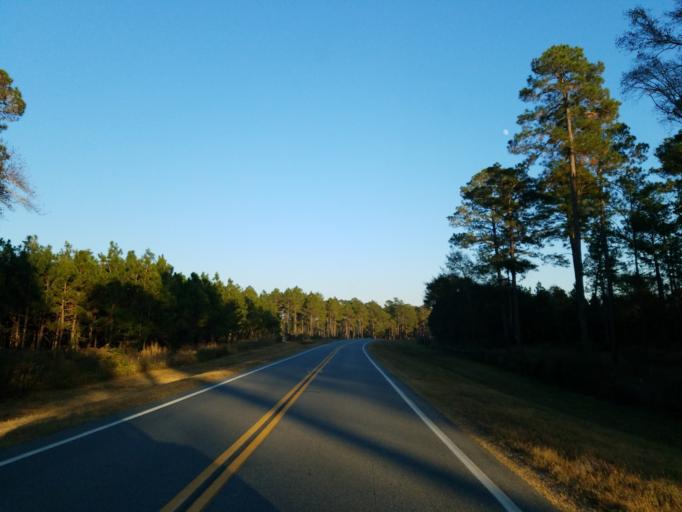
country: US
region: Georgia
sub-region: Turner County
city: Ashburn
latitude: 31.8239
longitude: -83.5512
